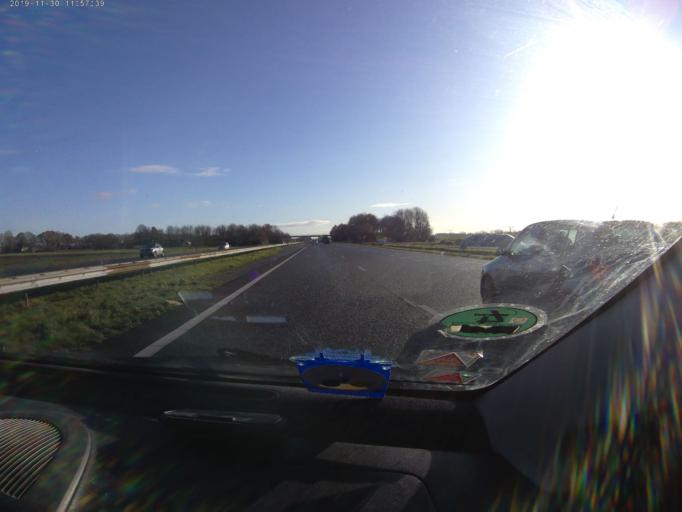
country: NL
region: Groningen
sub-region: Gemeente Hoogezand-Sappemeer
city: Hoogezand
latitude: 53.1918
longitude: 6.7066
